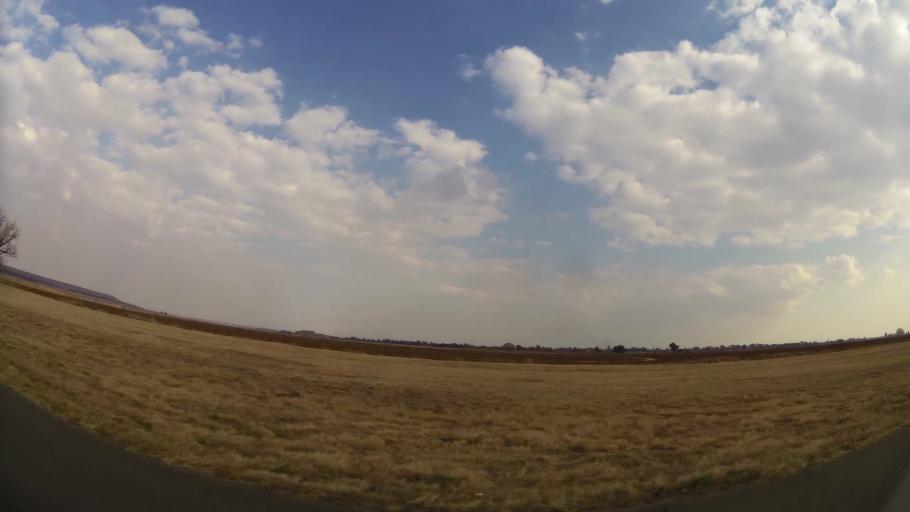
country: ZA
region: Gauteng
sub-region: Ekurhuleni Metropolitan Municipality
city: Springs
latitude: -26.2692
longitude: 28.4944
